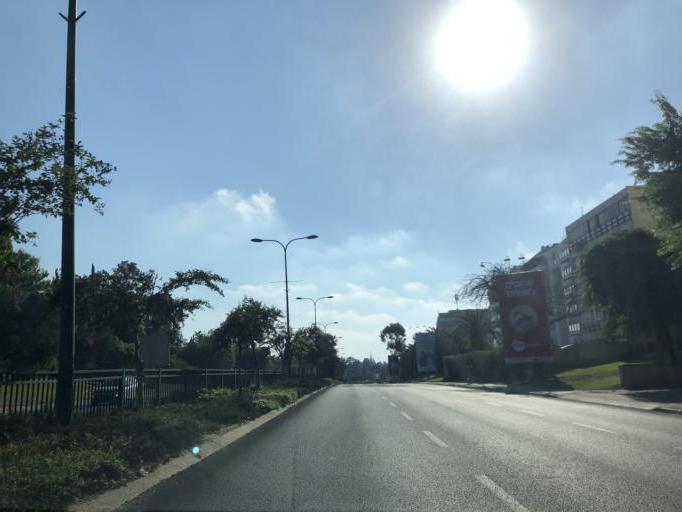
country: IL
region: Tel Aviv
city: Giv`atayim
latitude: 32.0593
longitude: 34.8191
